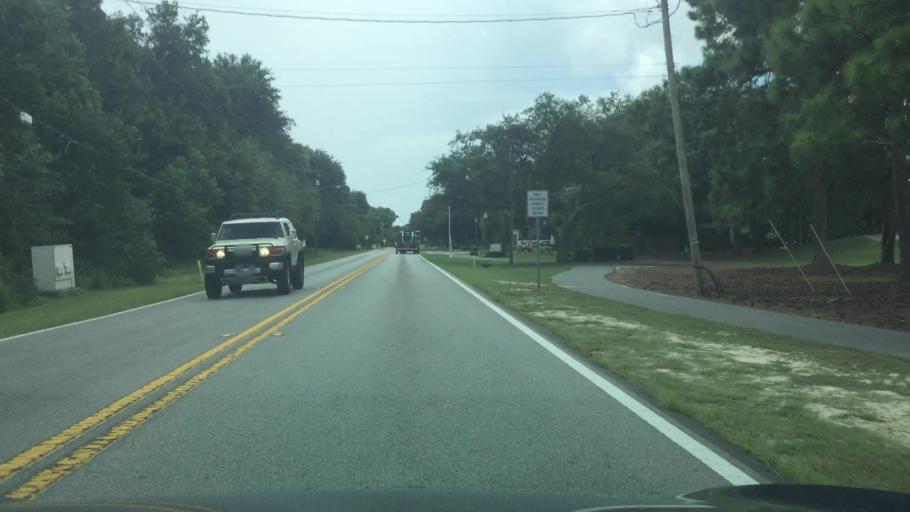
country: US
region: Florida
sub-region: Bay County
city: Upper Grand Lagoon
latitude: 30.1544
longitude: -85.7285
